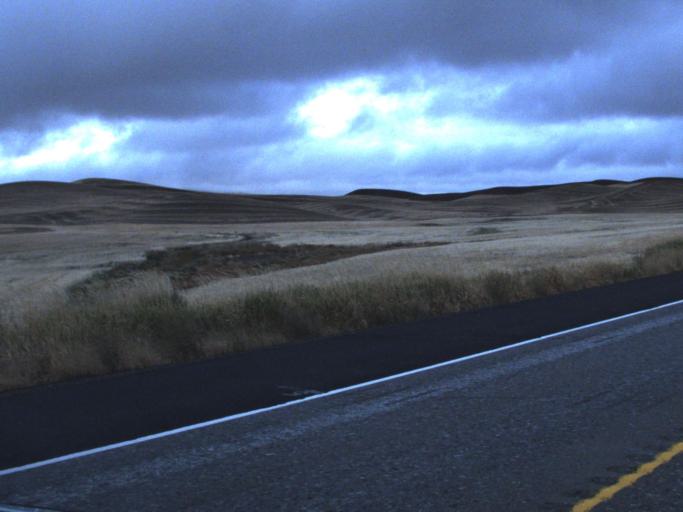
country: US
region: Washington
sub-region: Whitman County
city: Colfax
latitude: 47.0449
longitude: -117.3774
